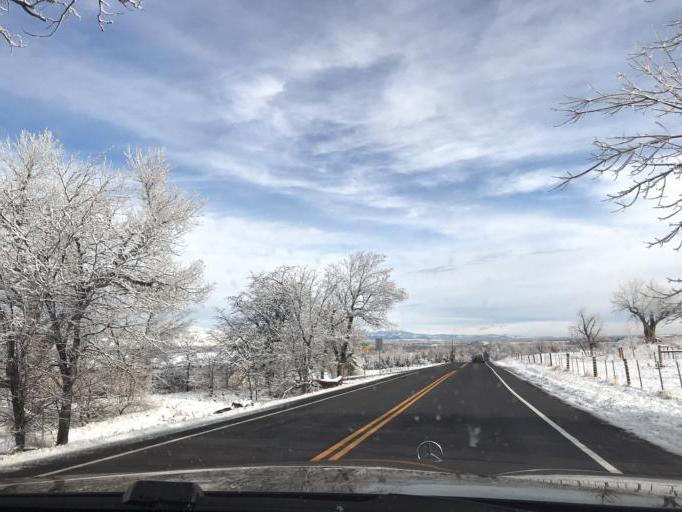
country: US
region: Colorado
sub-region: Boulder County
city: Superior
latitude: 39.9637
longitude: -105.2129
